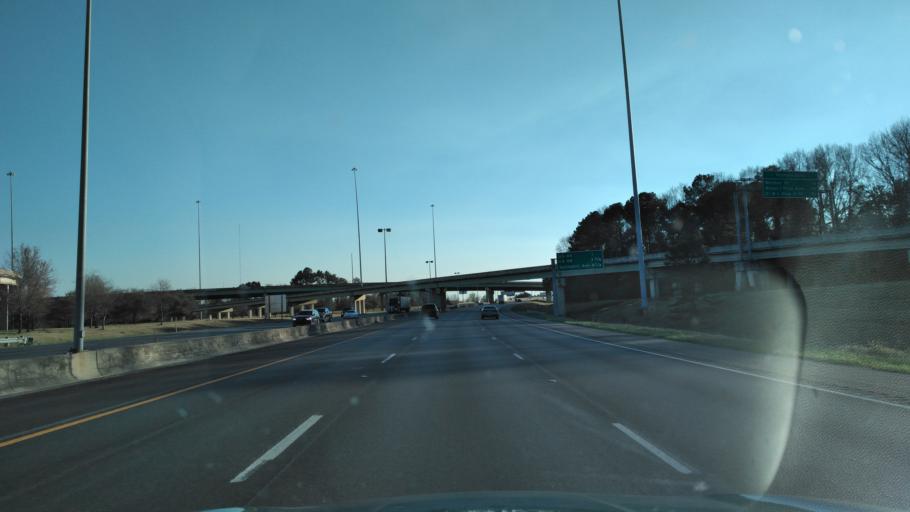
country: US
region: Alabama
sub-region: Mobile County
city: Chickasaw
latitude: 30.7556
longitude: -88.0936
